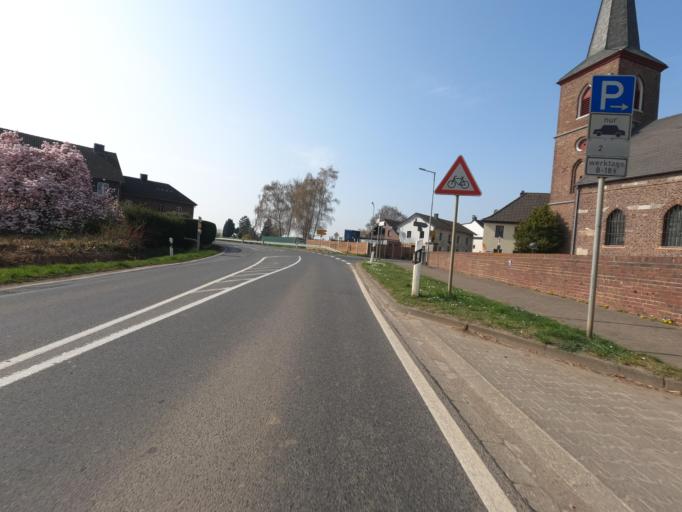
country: DE
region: North Rhine-Westphalia
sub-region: Regierungsbezirk Koln
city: Linnich
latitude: 50.9975
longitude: 6.3440
